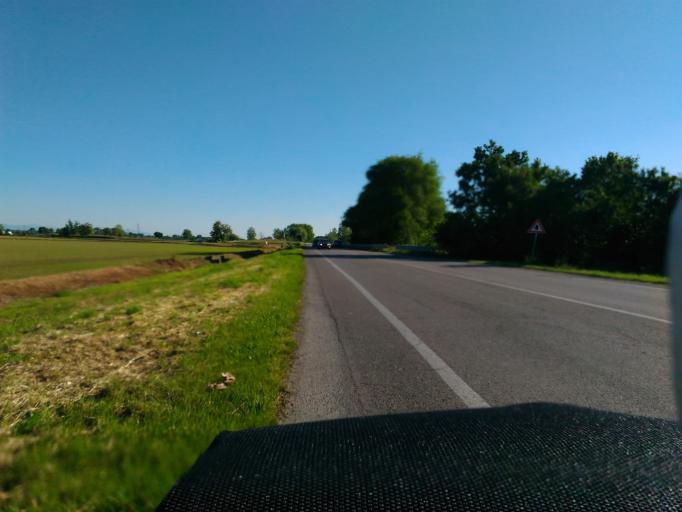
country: IT
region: Lombardy
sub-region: Citta metropolitana di Milano
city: Locate di Triulzi
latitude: 45.3669
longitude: 9.2491
